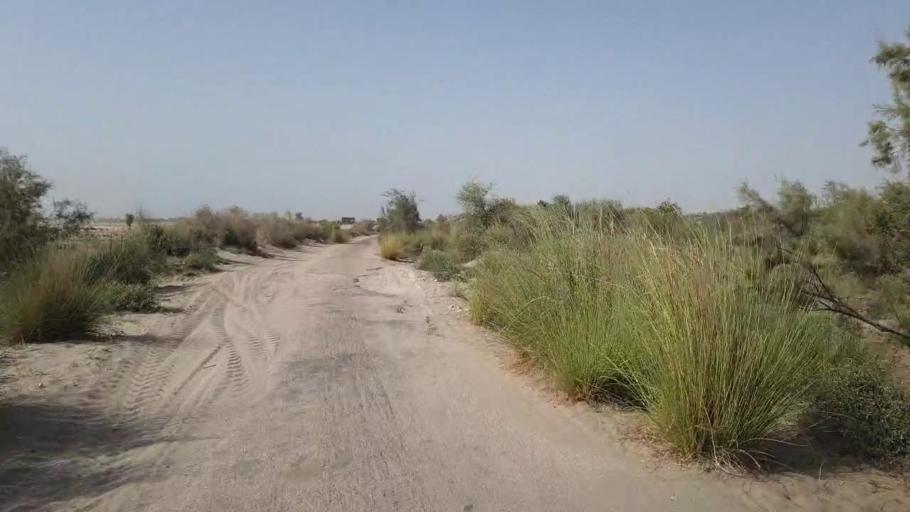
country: PK
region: Sindh
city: Jam Sahib
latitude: 26.5968
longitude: 68.9233
